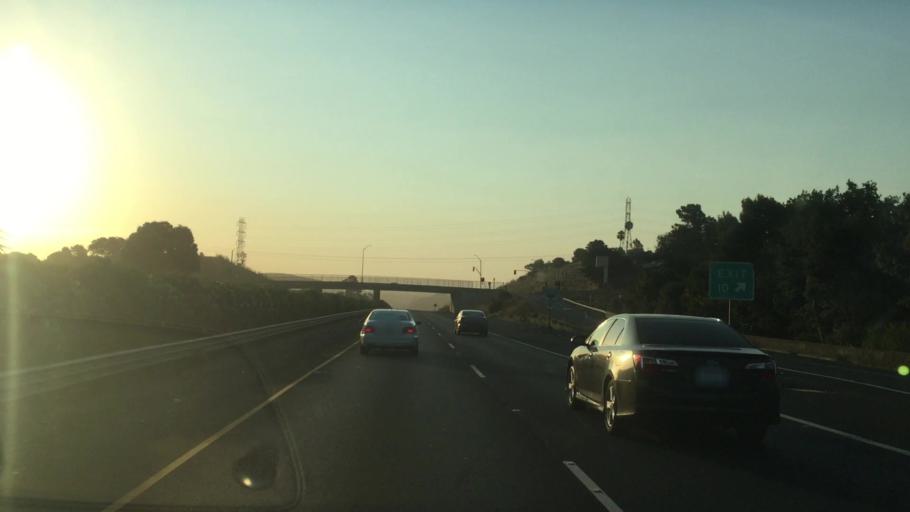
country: US
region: California
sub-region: Contra Costa County
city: Crockett
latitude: 38.0861
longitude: -122.2131
